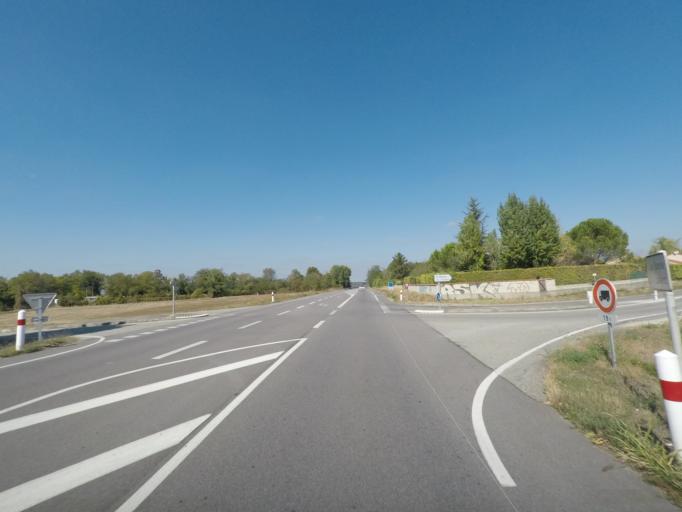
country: FR
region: Rhone-Alpes
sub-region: Departement de la Drome
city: Chabeuil
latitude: 44.8955
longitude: 5.0108
